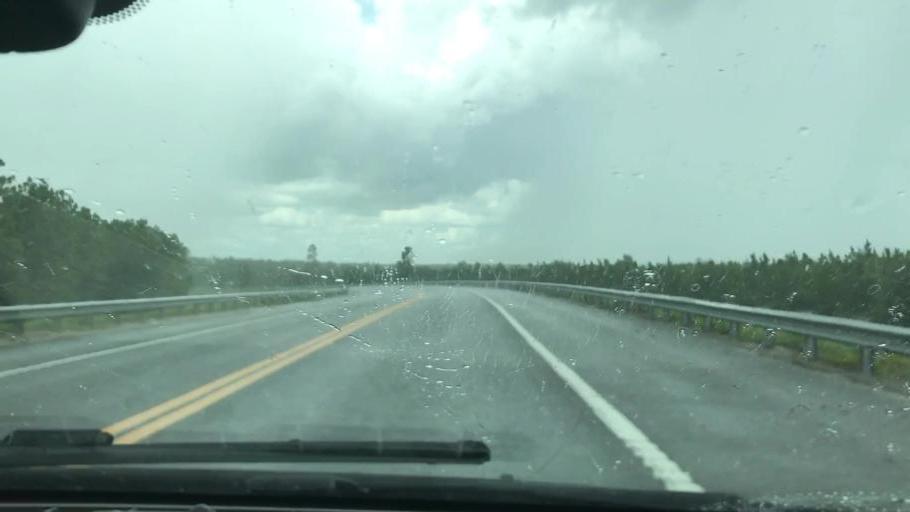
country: US
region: Florida
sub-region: Madison County
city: Madison
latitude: 30.3975
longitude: -83.2058
